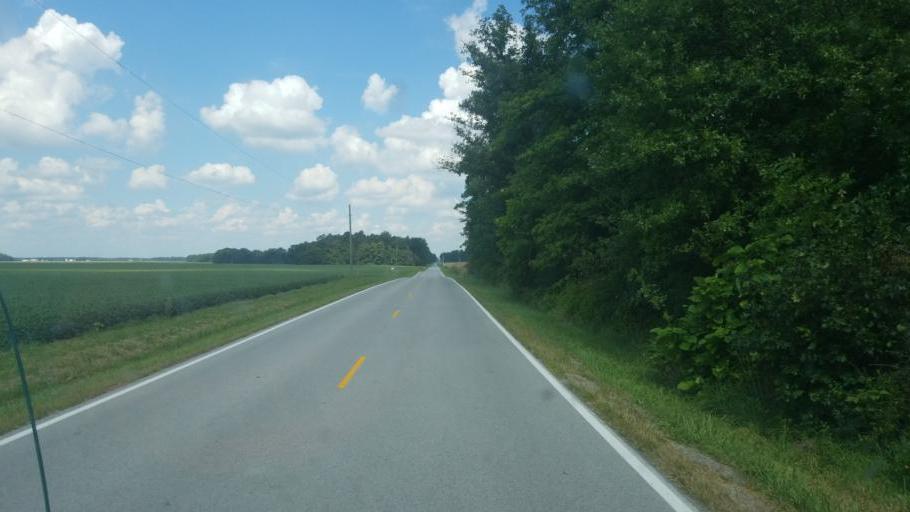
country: US
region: Ohio
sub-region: Hancock County
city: Arlington
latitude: 40.8365
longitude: -83.7277
